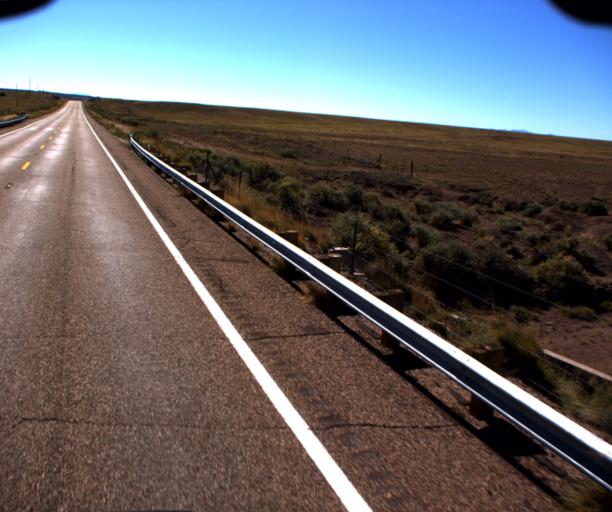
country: US
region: Arizona
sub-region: Apache County
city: Saint Johns
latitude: 34.5251
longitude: -109.4559
